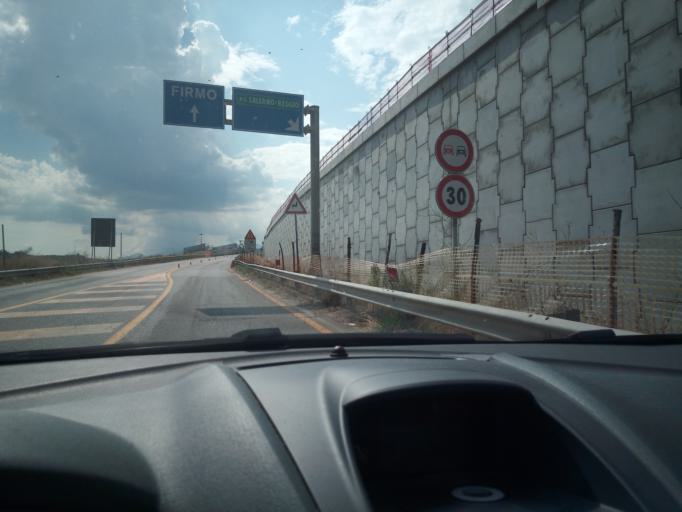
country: IT
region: Calabria
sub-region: Provincia di Cosenza
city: San Lorenzo del Vallo
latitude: 39.7215
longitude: 16.2423
